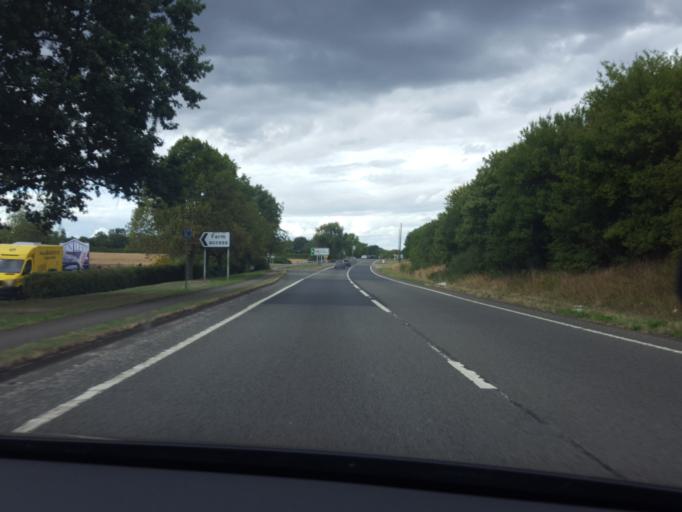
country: GB
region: England
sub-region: Leicestershire
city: Mountsorrel
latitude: 52.6973
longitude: -1.1264
